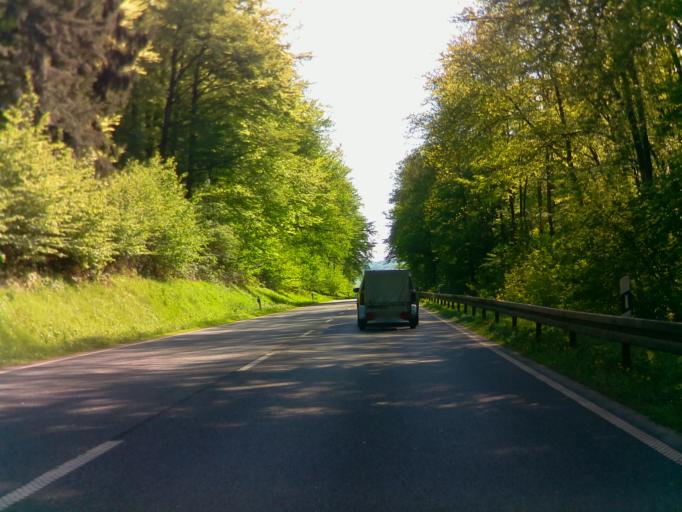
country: DE
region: Hesse
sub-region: Regierungsbezirk Darmstadt
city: Wachtersbach
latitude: 50.2454
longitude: 9.2965
